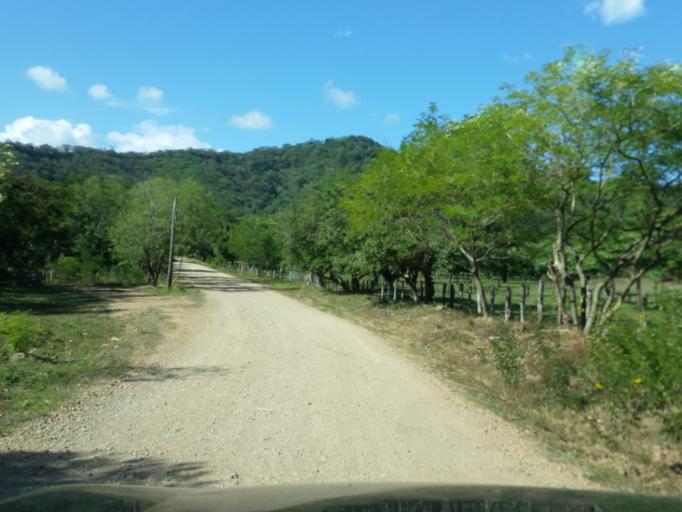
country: NI
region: Rivas
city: San Juan del Sur
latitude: 11.1719
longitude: -85.7990
